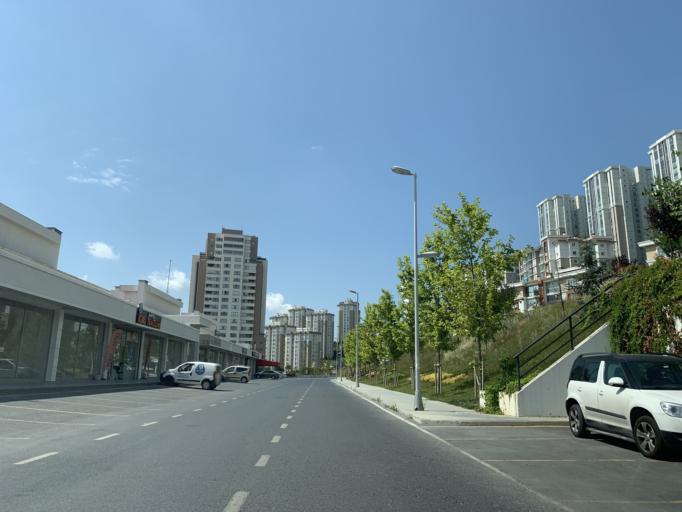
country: TR
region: Istanbul
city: Esenyurt
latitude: 41.0764
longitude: 28.6945
